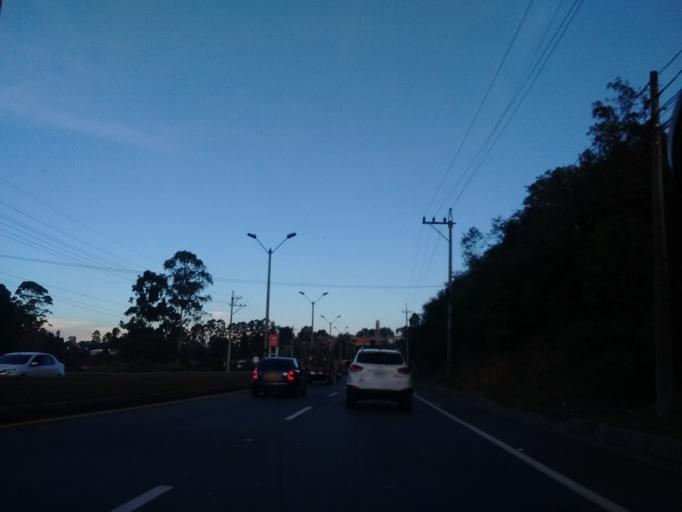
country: CO
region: Antioquia
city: Rionegro
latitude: 6.1812
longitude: -75.3705
